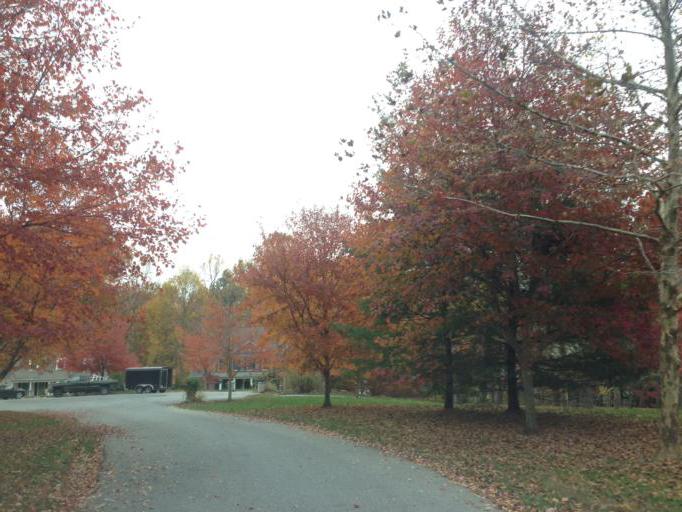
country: US
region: Maryland
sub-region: Howard County
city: Highland
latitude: 39.2778
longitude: -76.9357
